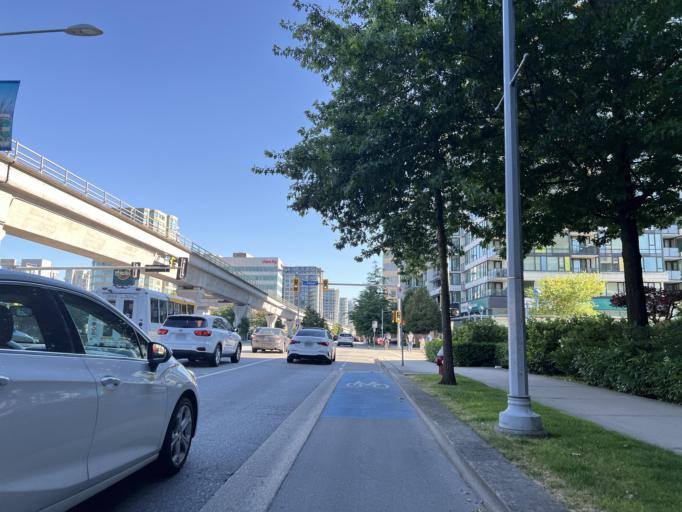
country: CA
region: British Columbia
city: Richmond
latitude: 49.1724
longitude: -123.1368
